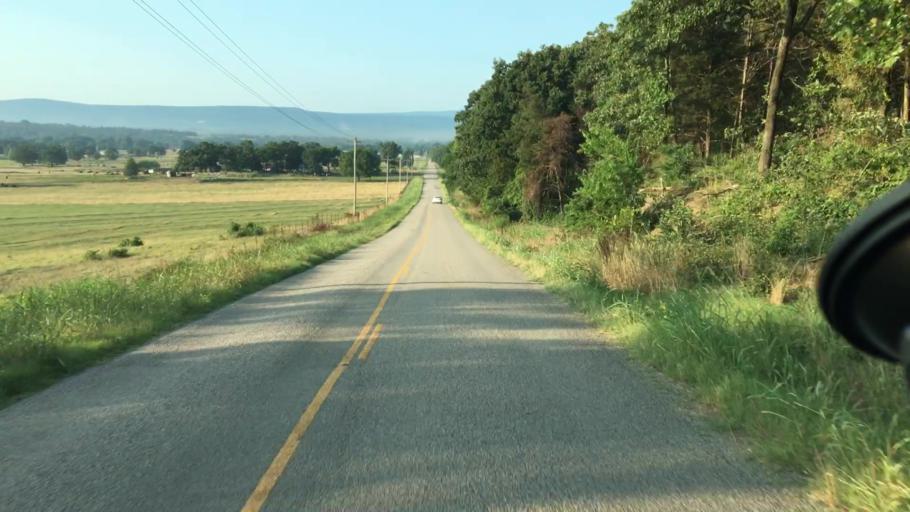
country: US
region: Arkansas
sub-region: Johnson County
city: Coal Hill
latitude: 35.3501
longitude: -93.6134
